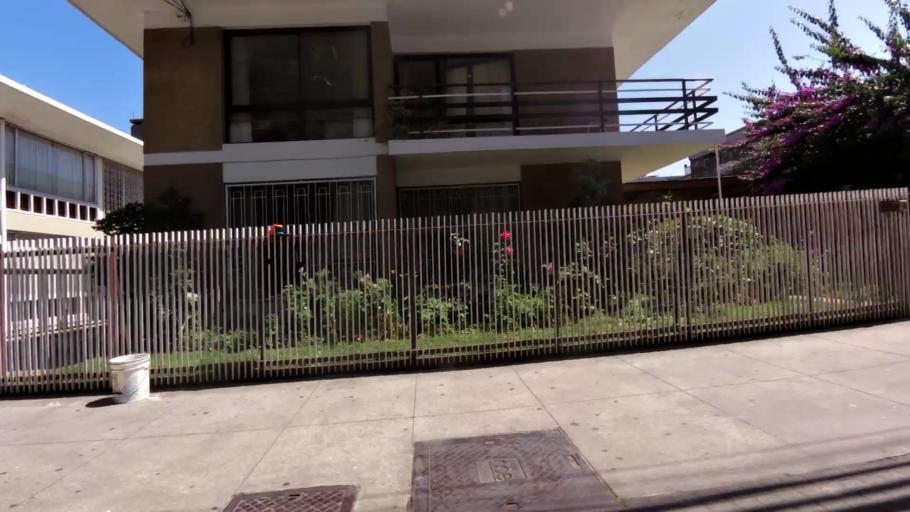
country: CL
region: Biobio
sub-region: Provincia de Concepcion
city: Concepcion
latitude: -36.8283
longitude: -73.0471
